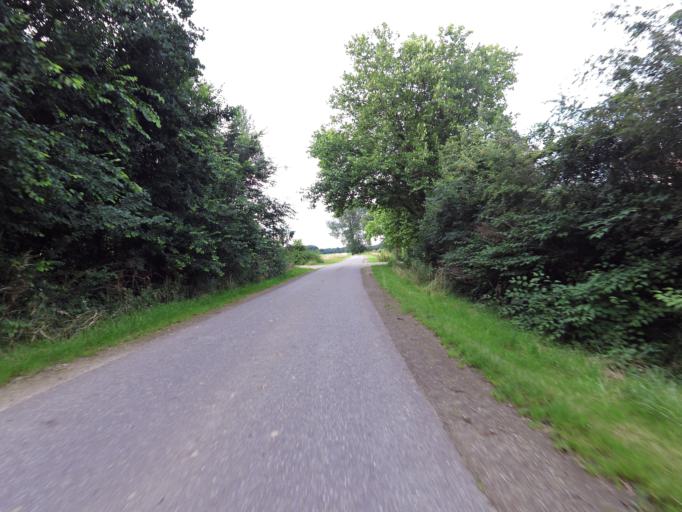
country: NL
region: Gelderland
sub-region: Gemeente Doesburg
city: Doesburg
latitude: 51.9853
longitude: 6.1855
